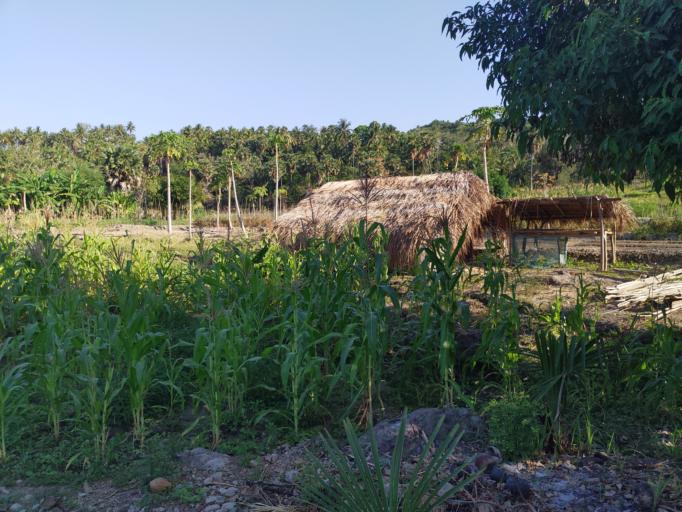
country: TL
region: Baucau
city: Baucau
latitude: -8.4434
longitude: 126.4690
